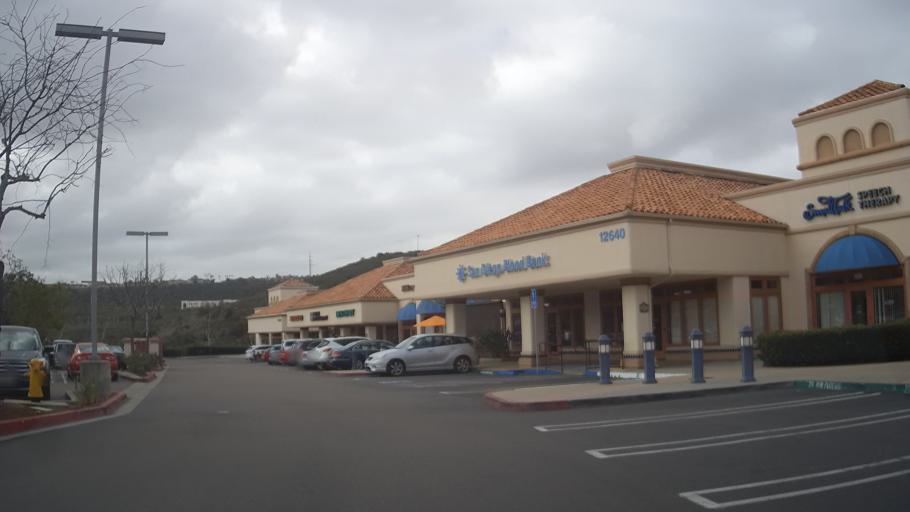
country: US
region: California
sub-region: San Diego County
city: Poway
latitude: 32.9482
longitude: -117.0967
